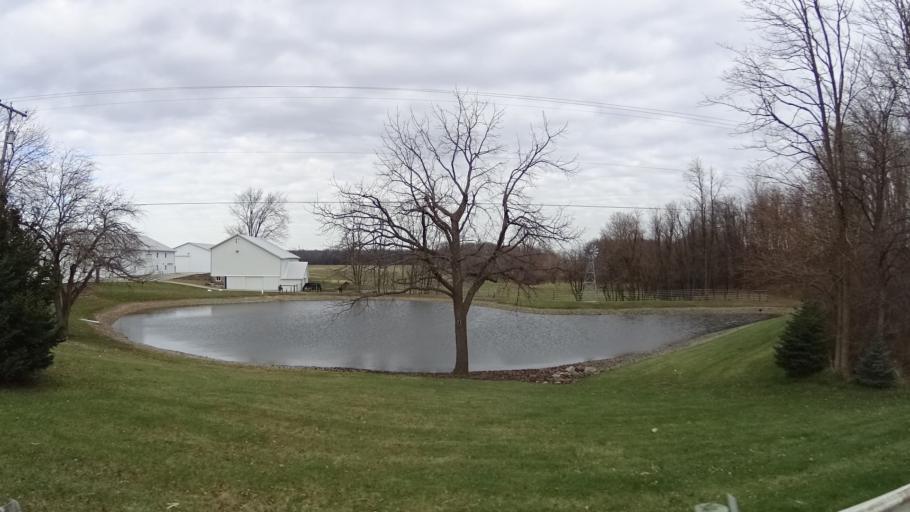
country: US
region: Ohio
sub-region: Lorain County
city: Camden
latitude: 41.2378
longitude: -82.3378
